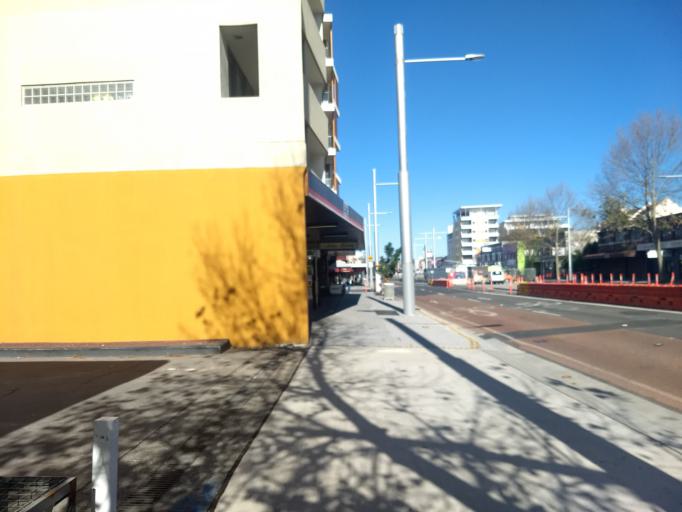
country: AU
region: New South Wales
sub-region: Randwick
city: Kensington
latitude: -33.9074
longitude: 151.2239
